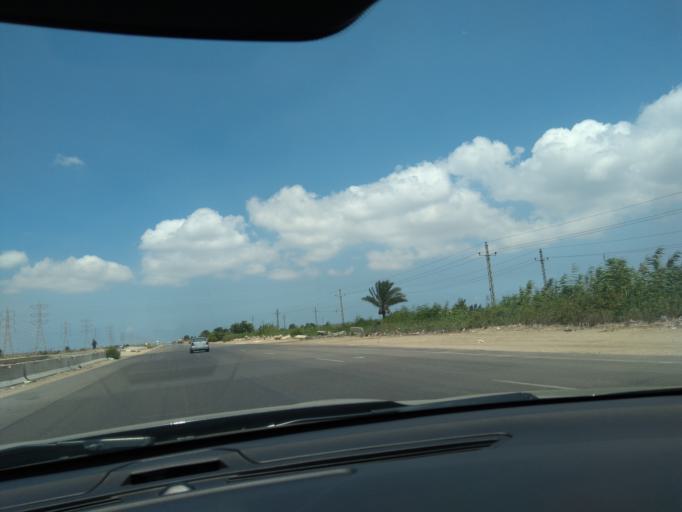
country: EG
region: Muhafazat Bur Sa`id
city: Port Said
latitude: 31.1602
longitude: 32.3019
